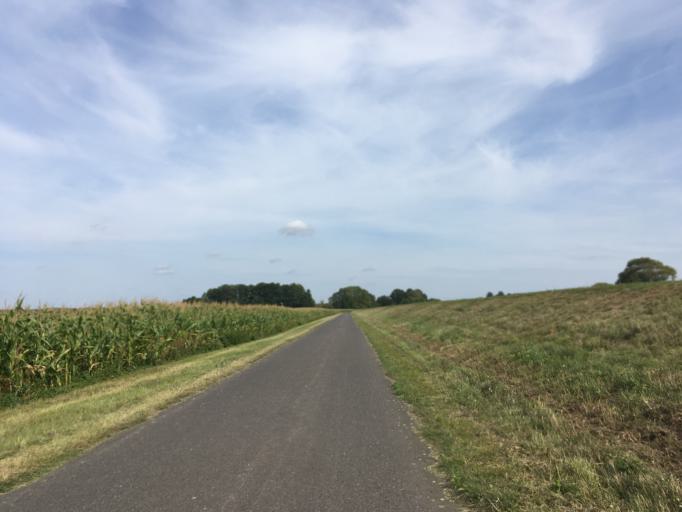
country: DE
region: Brandenburg
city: Schenkendobern
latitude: 51.8689
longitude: 14.6430
